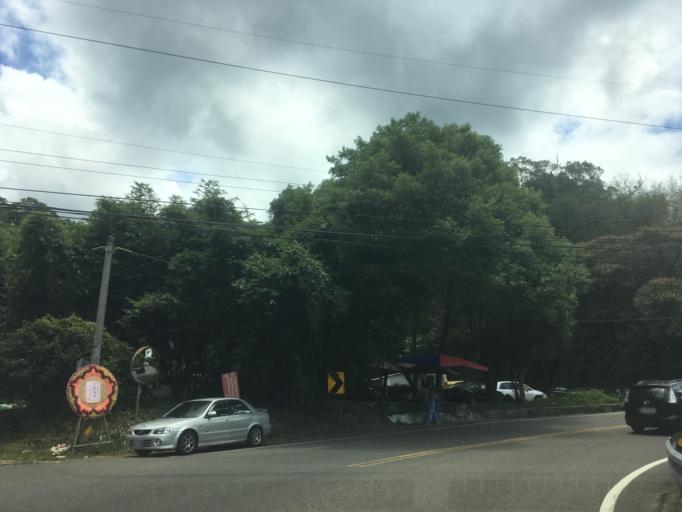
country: TW
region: Taiwan
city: Daxi
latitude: 24.8295
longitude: 121.3361
